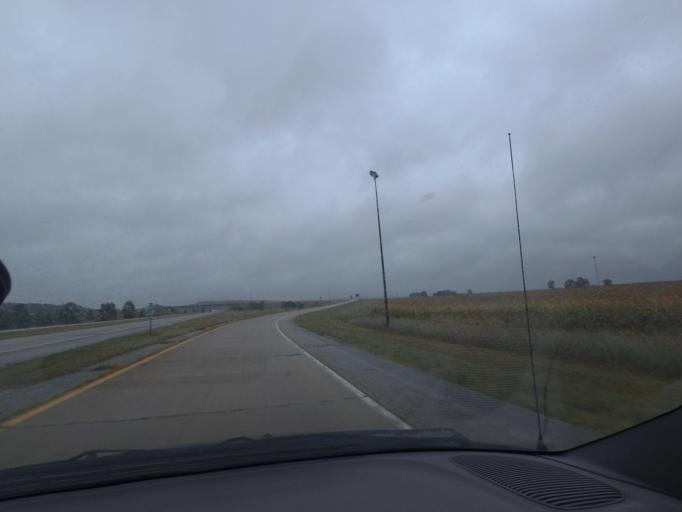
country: US
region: Illinois
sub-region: Adams County
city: Payson
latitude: 39.7190
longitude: -91.1989
